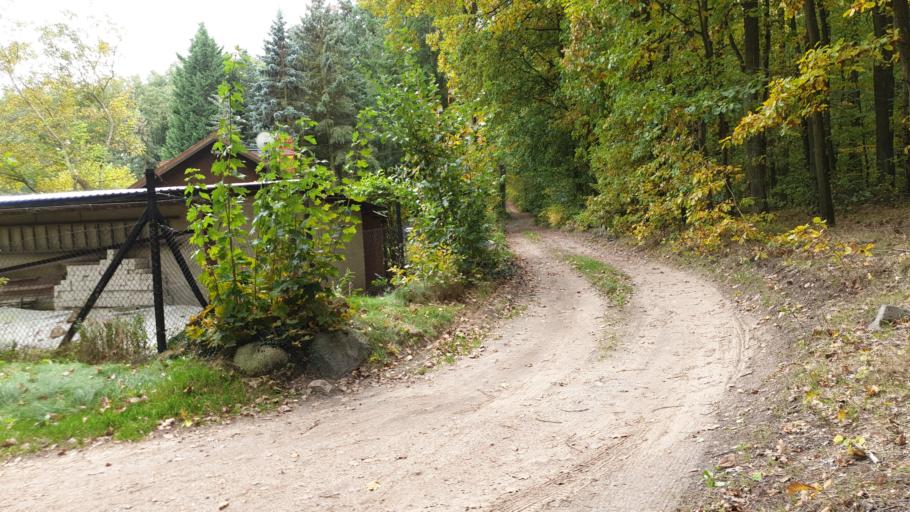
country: DE
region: Brandenburg
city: Liepe
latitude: 52.8631
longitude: 13.9463
